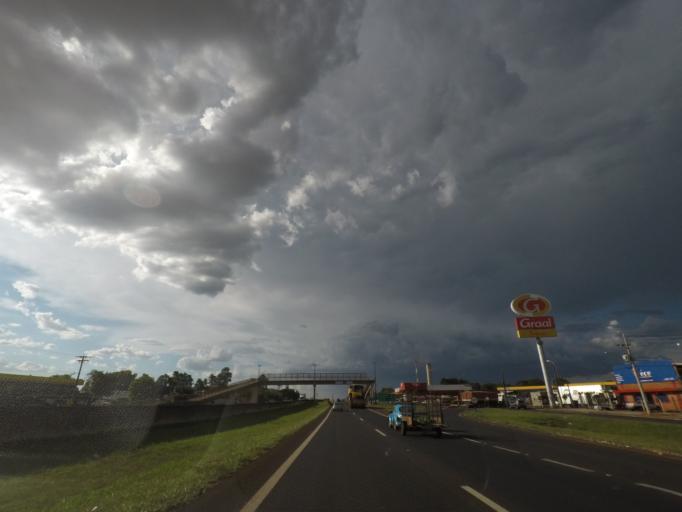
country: BR
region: Sao Paulo
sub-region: Ribeirao Preto
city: Ribeirao Preto
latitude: -21.1033
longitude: -47.7869
